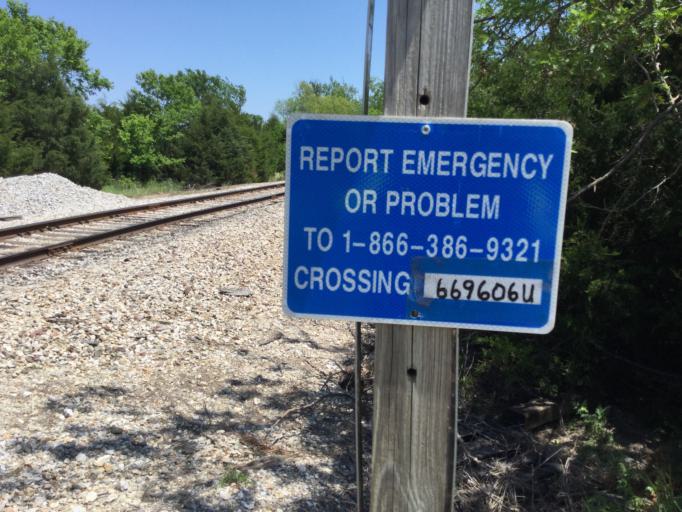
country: US
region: Kansas
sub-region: Montgomery County
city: Cherryvale
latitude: 37.2578
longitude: -95.4814
